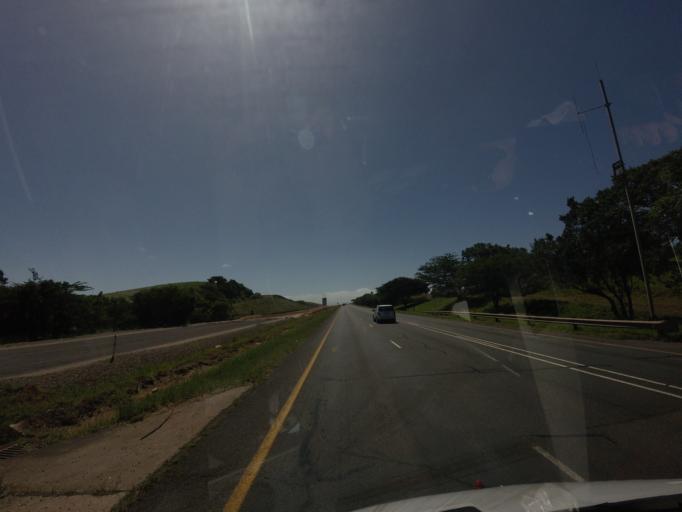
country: ZA
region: KwaZulu-Natal
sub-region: uThungulu District Municipality
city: eSikhawini
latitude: -28.9308
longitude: 31.7706
